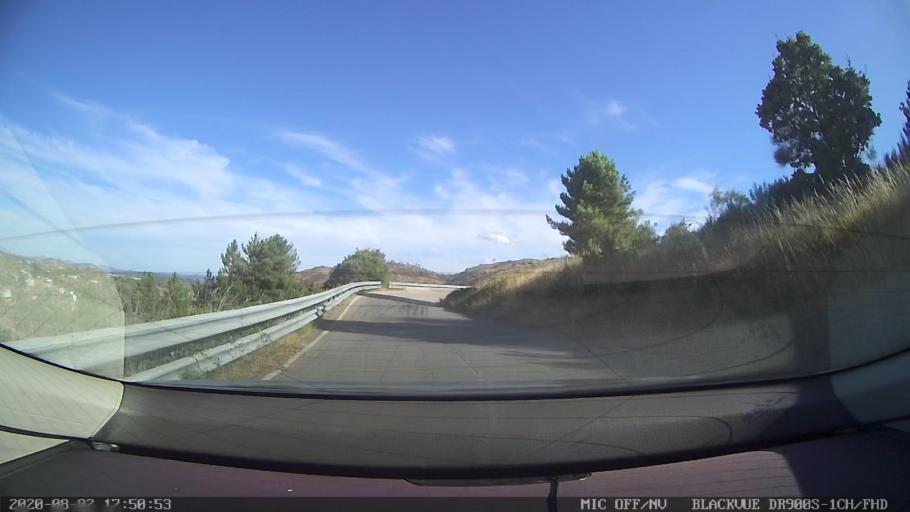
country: PT
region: Vila Real
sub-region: Murca
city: Murca
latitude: 41.4024
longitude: -7.4711
